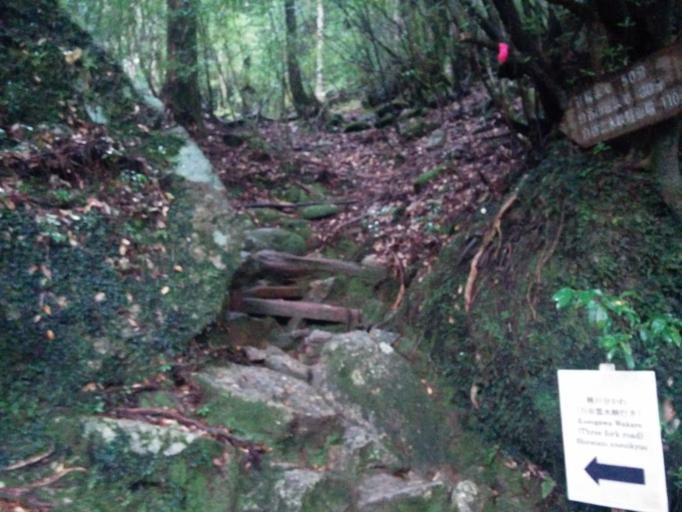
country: JP
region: Kagoshima
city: Nishinoomote
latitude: 30.3542
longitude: 130.5628
